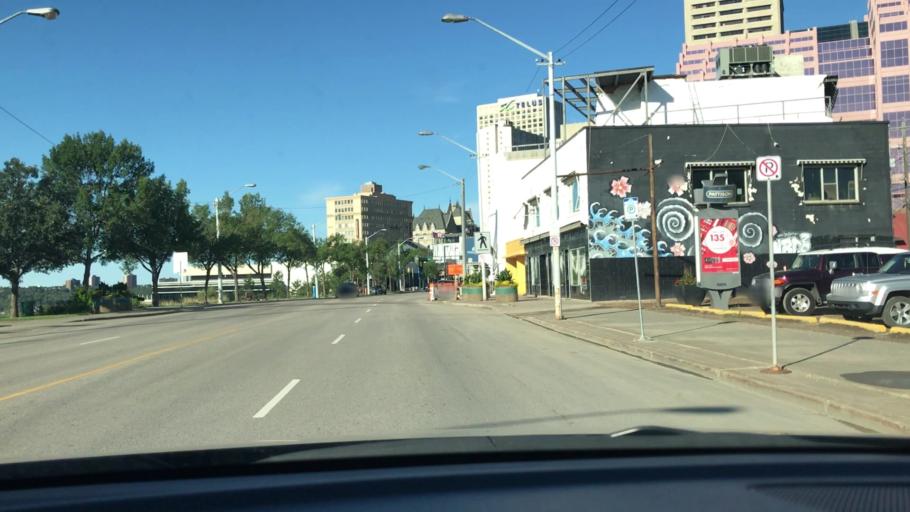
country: CA
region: Alberta
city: Edmonton
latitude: 53.5432
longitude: -113.4831
